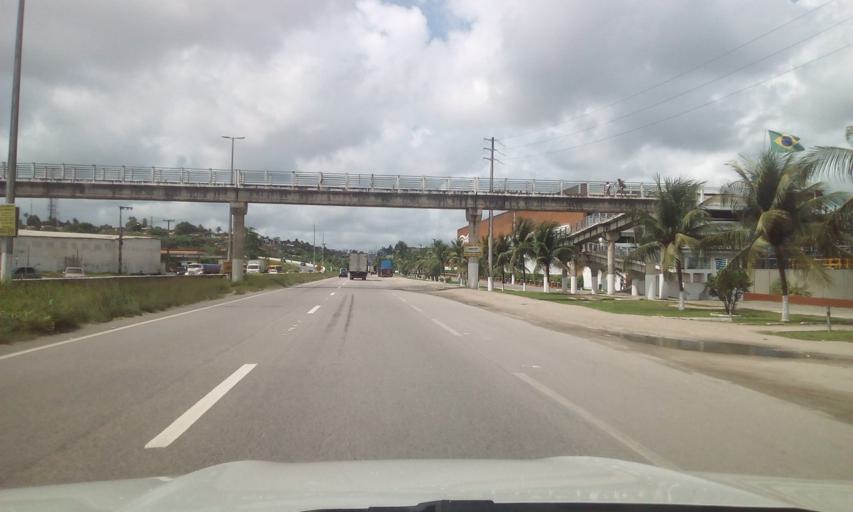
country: BR
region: Pernambuco
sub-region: Igarassu
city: Igarassu
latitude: -7.8303
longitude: -34.9143
